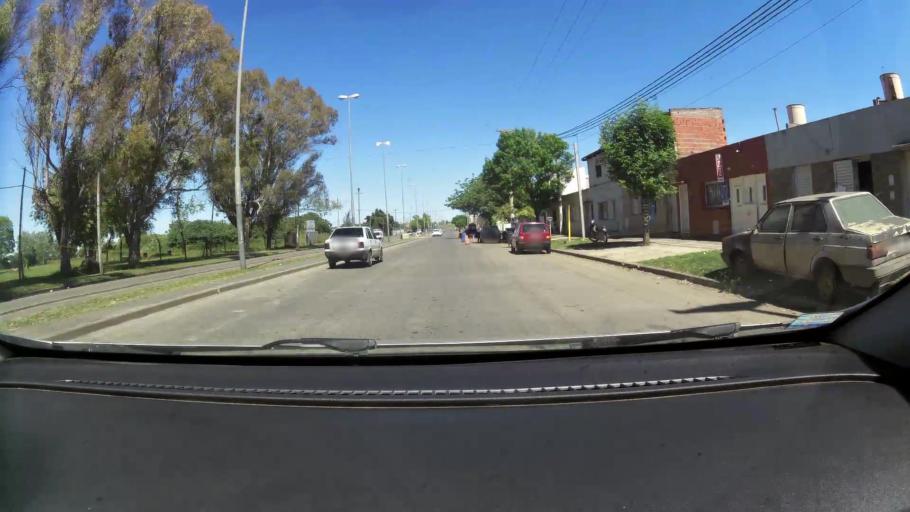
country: AR
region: Santa Fe
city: Perez
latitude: -32.9709
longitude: -60.7072
